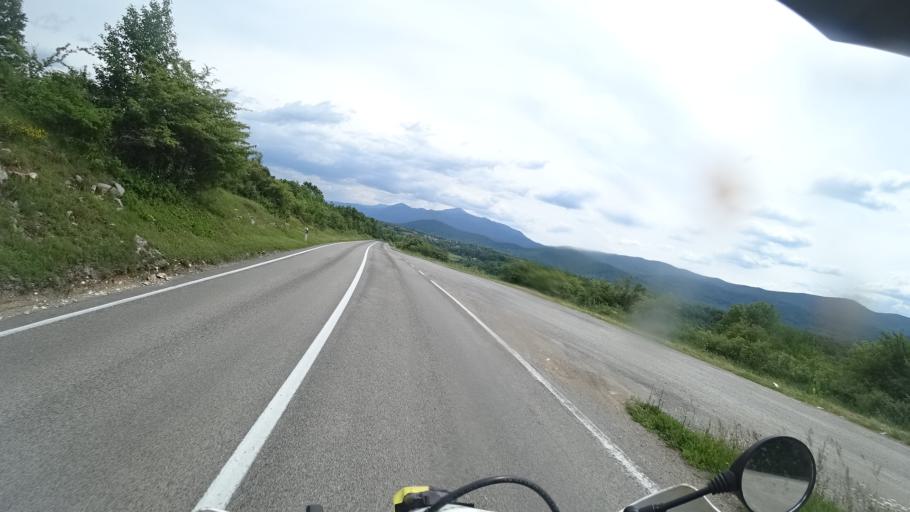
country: HR
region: Licko-Senjska
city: Jezerce
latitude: 44.9267
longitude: 15.7024
